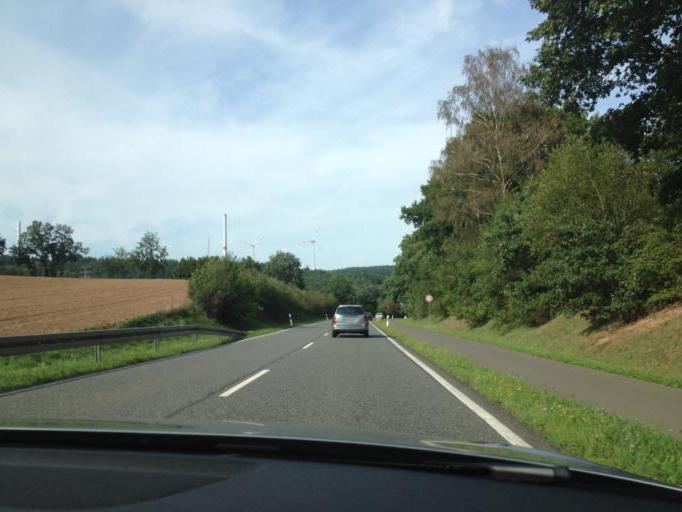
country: DE
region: Saarland
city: Hangard
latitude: 49.4215
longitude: 7.2136
